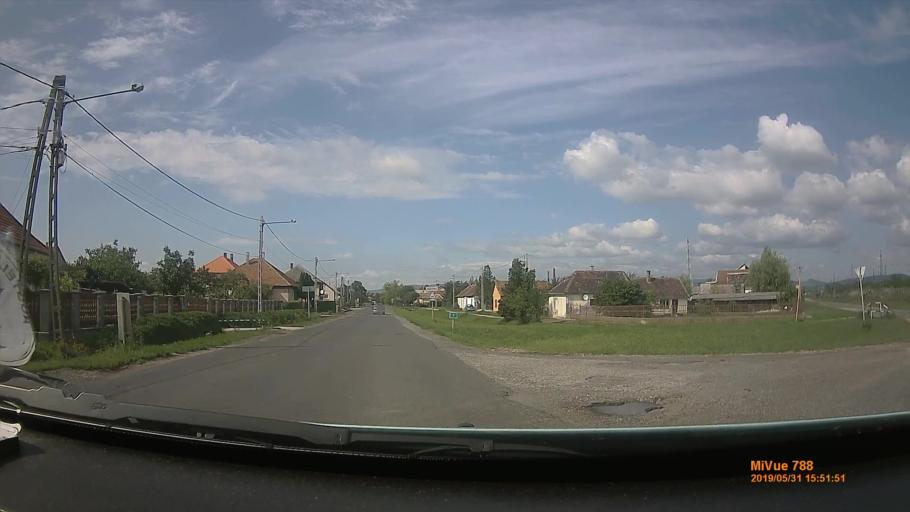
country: HU
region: Borsod-Abauj-Zemplen
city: Szerencs
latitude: 48.1471
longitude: 21.2007
